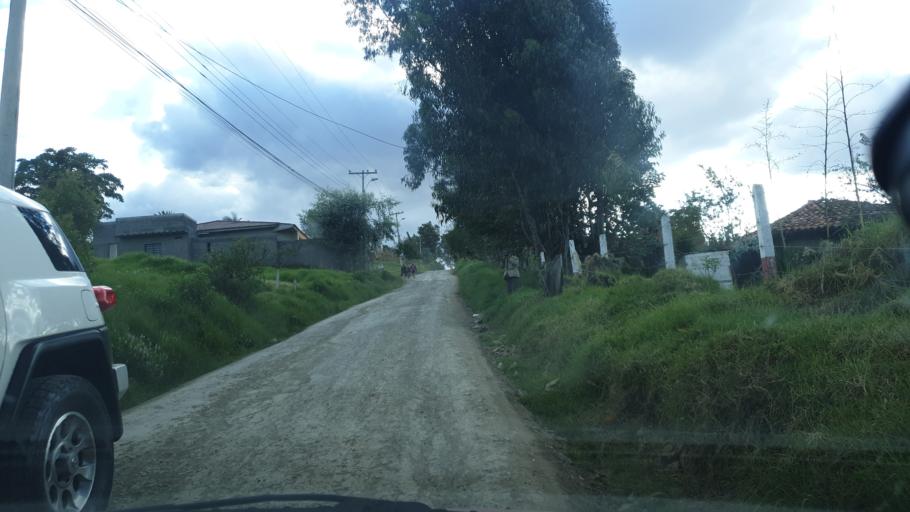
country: EC
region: Azuay
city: Cuenca
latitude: -2.9251
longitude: -78.9663
